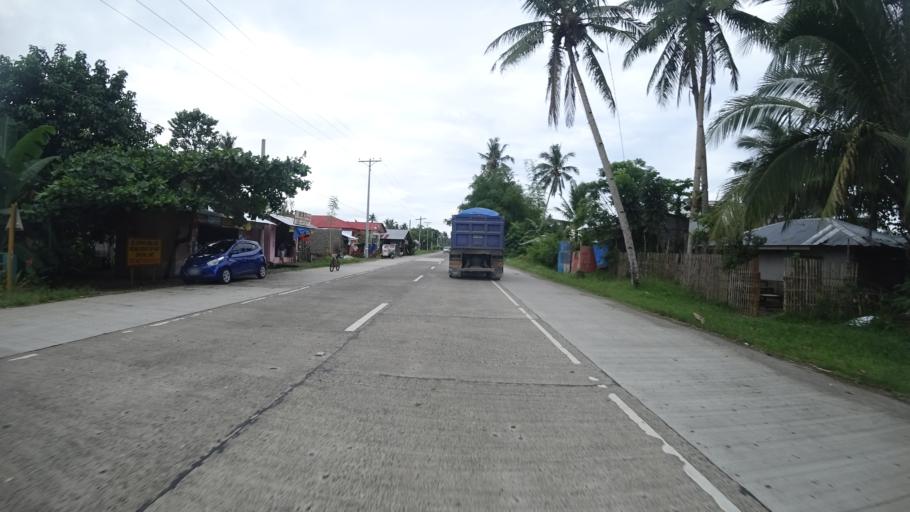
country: PH
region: Eastern Visayas
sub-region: Province of Leyte
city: MacArthur
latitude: 10.8475
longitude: 124.9949
